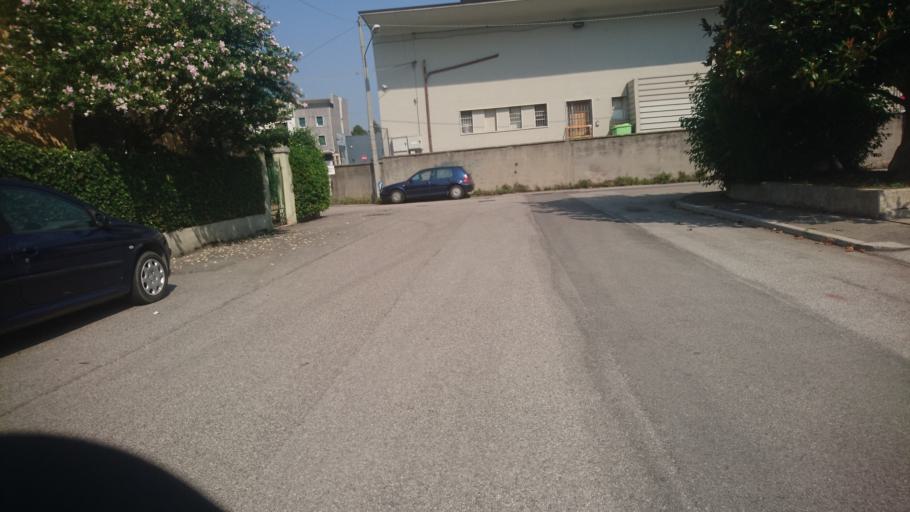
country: IT
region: Veneto
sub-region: Provincia di Padova
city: Padova
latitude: 45.4088
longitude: 11.9049
